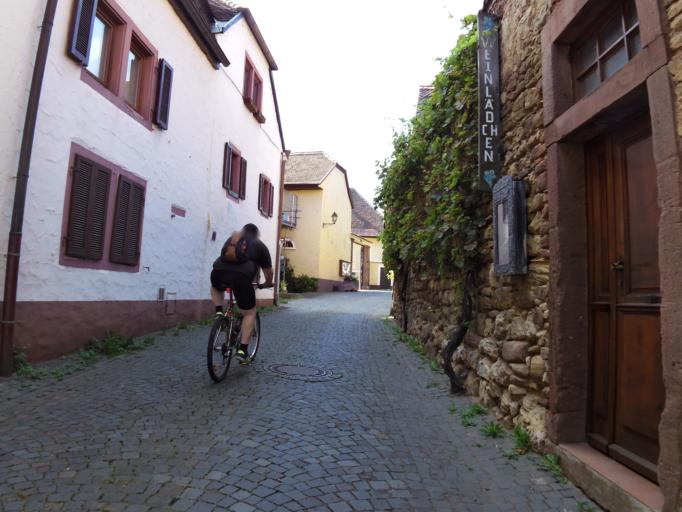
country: DE
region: Rheinland-Pfalz
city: Neuleiningen
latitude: 49.5423
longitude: 8.1389
